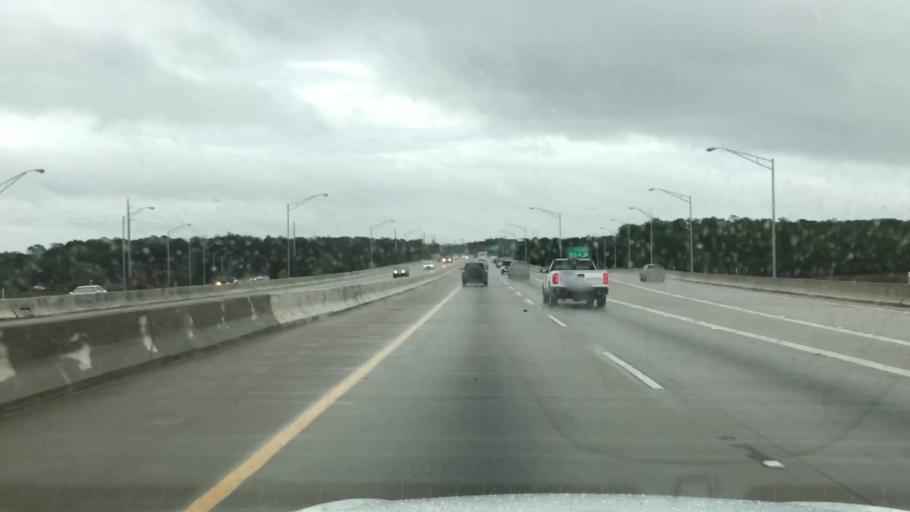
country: US
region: South Carolina
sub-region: Charleston County
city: North Charleston
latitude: 32.8815
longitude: -79.9349
